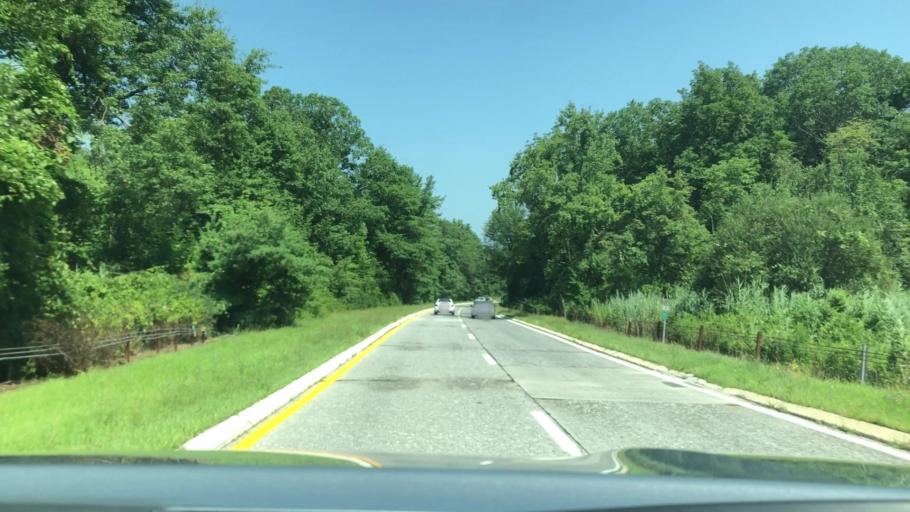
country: US
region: New York
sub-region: Rockland County
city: Stony Point
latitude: 41.2765
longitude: -74.0308
